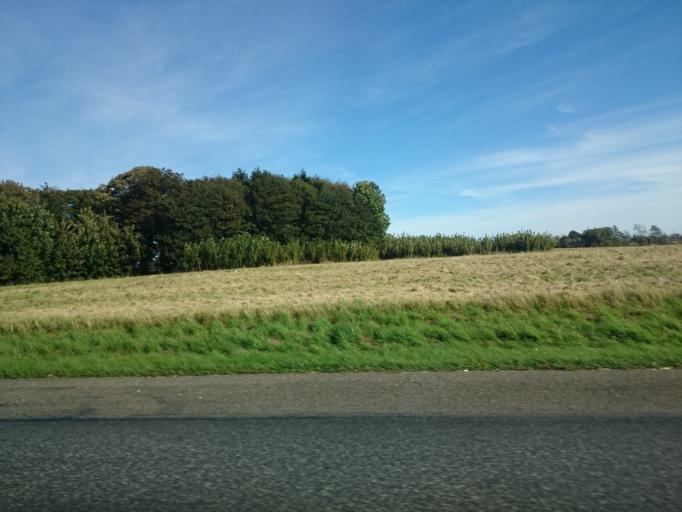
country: DK
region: Central Jutland
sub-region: Horsens Kommune
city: Horsens
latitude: 55.9288
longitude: 9.8196
